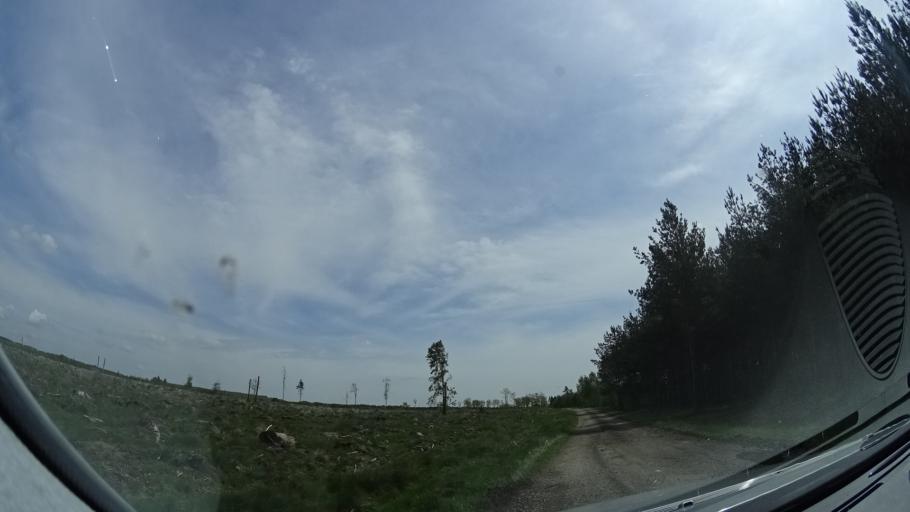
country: SE
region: Skane
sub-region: Sjobo Kommun
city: Sjoebo
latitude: 55.6668
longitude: 13.6523
